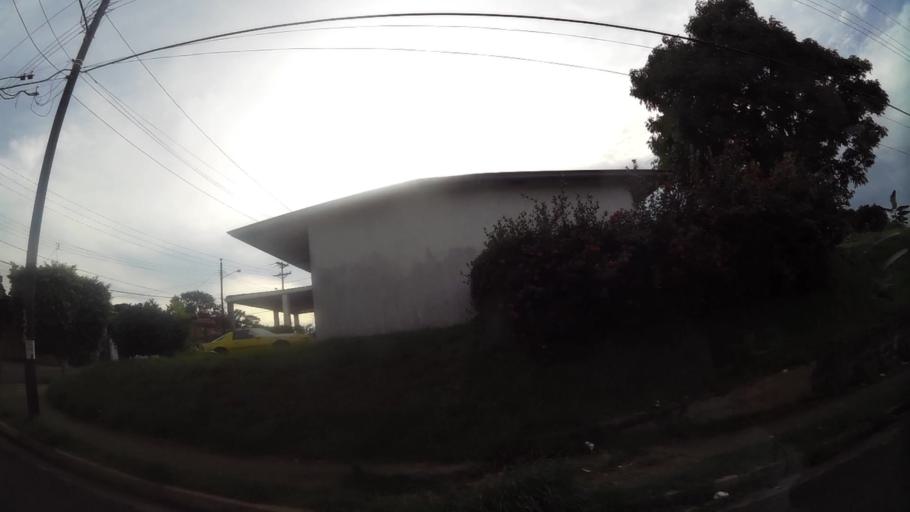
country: PA
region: Panama
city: La Chorrera
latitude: 8.8912
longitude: -79.7717
